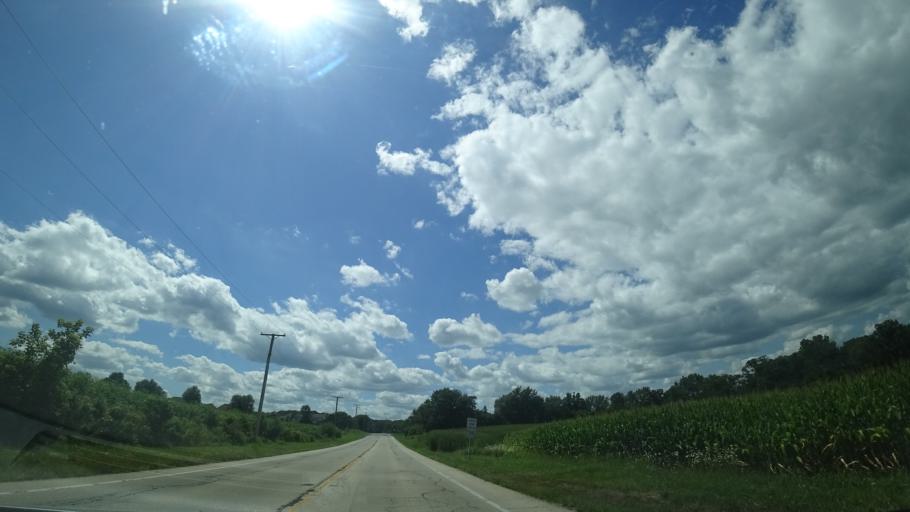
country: US
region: Illinois
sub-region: Will County
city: Homer Glen
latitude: 41.5859
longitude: -87.9085
